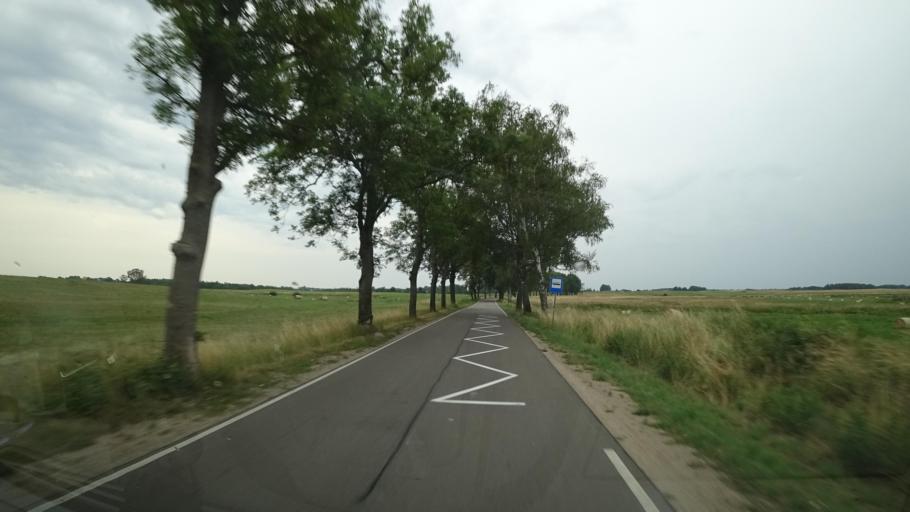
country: PL
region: Warmian-Masurian Voivodeship
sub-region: Powiat mragowski
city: Mikolajki
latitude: 53.8729
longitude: 21.5957
